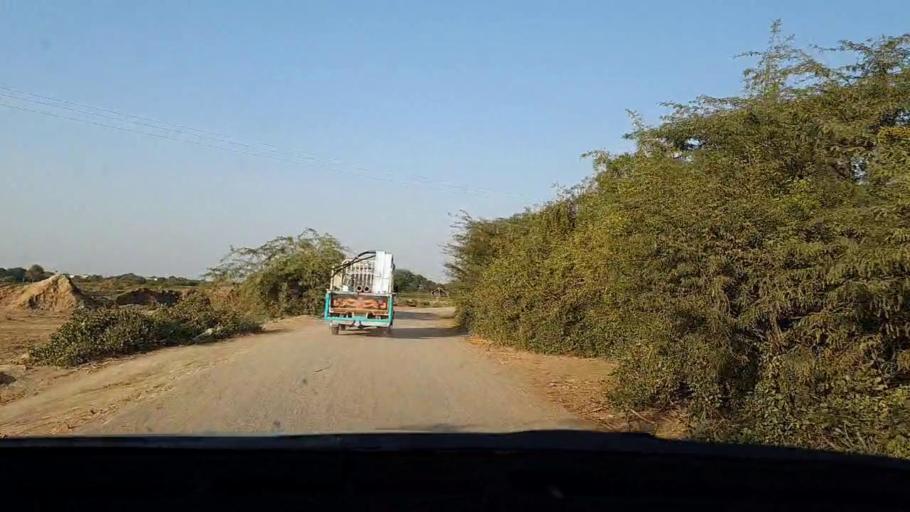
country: PK
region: Sindh
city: Tando Mittha Khan
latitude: 25.8638
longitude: 69.3054
